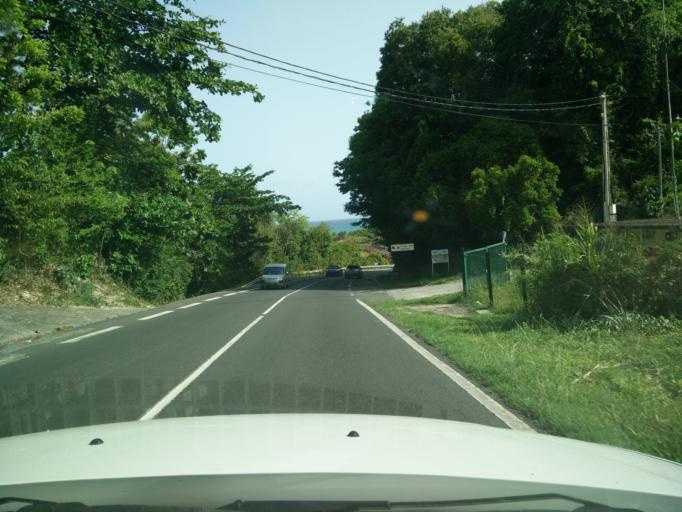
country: GP
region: Guadeloupe
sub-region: Guadeloupe
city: Le Gosier
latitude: 16.2088
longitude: -61.4420
